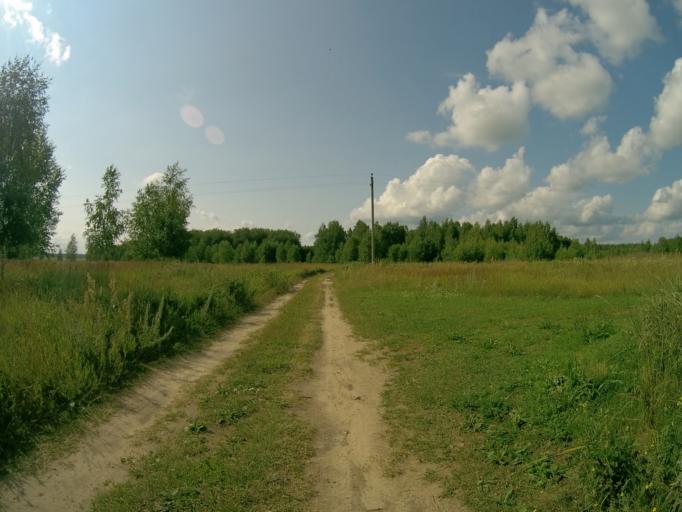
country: RU
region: Vladimir
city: Orgtrud
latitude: 56.2782
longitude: 40.7021
